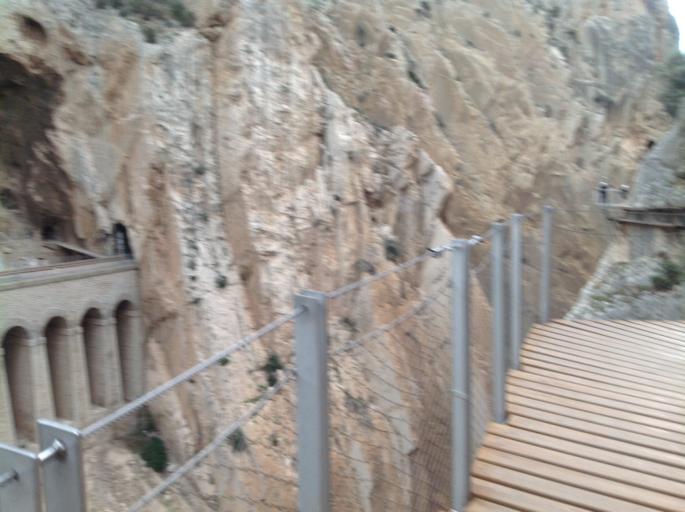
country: ES
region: Andalusia
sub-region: Provincia de Malaga
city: Carratraca
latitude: 36.9171
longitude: -4.7740
